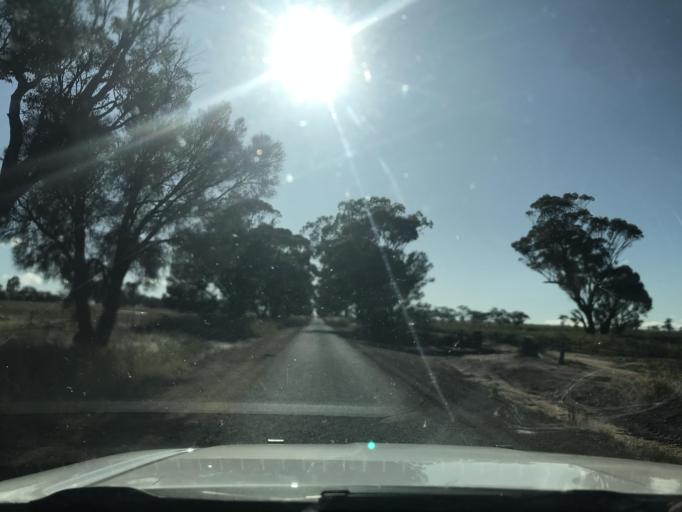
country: AU
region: Victoria
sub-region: Horsham
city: Horsham
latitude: -36.6944
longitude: 141.5673
